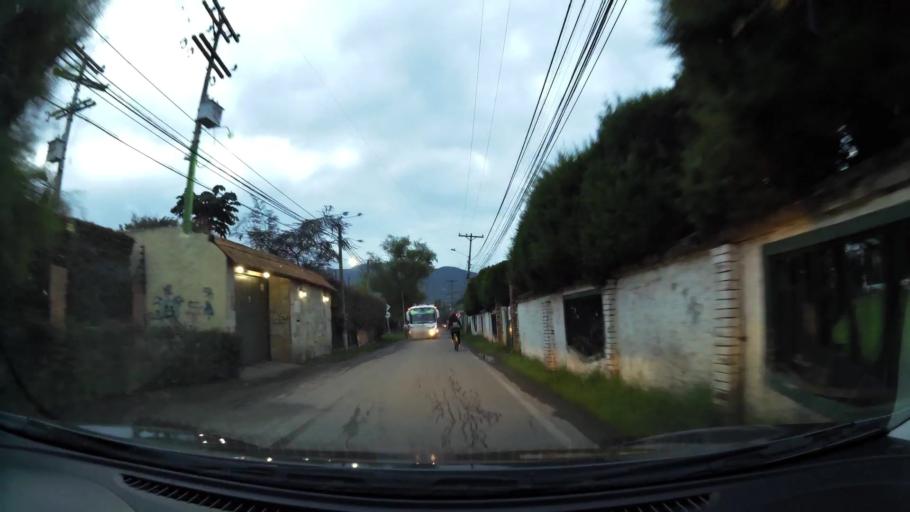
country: CO
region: Cundinamarca
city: Chia
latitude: 4.8418
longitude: -74.0683
